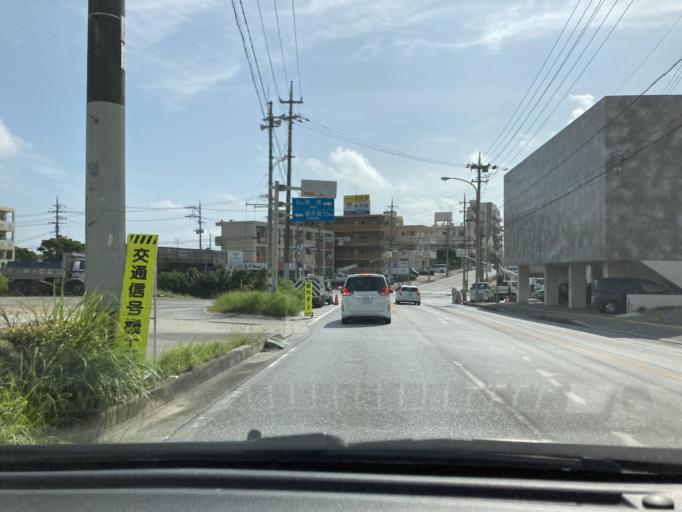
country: JP
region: Okinawa
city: Ginowan
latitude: 26.2545
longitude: 127.7736
